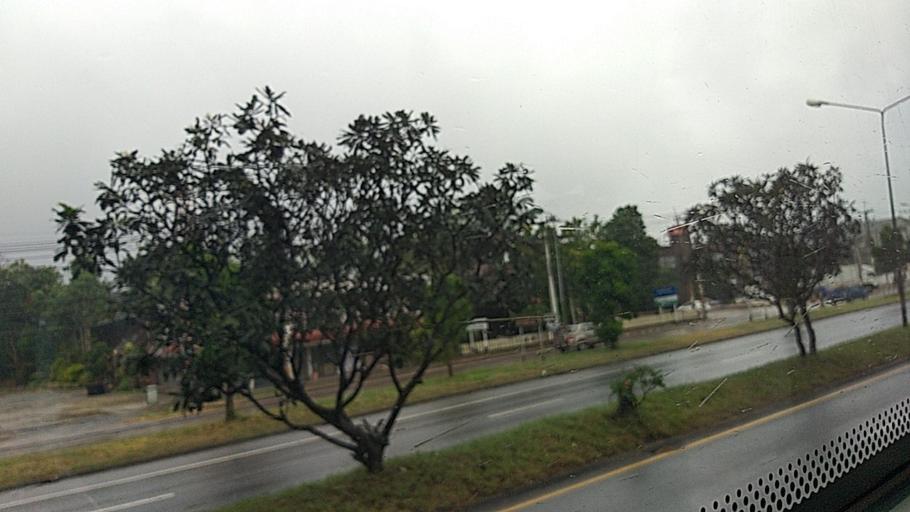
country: TH
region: Nakhon Ratchasima
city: Sung Noen
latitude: 14.8698
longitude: 101.8312
